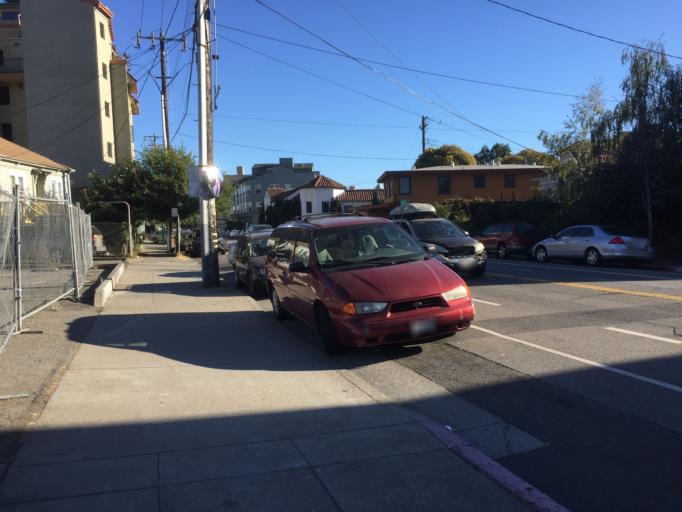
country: US
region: California
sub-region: Alameda County
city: Emeryville
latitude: 37.8358
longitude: -122.2639
